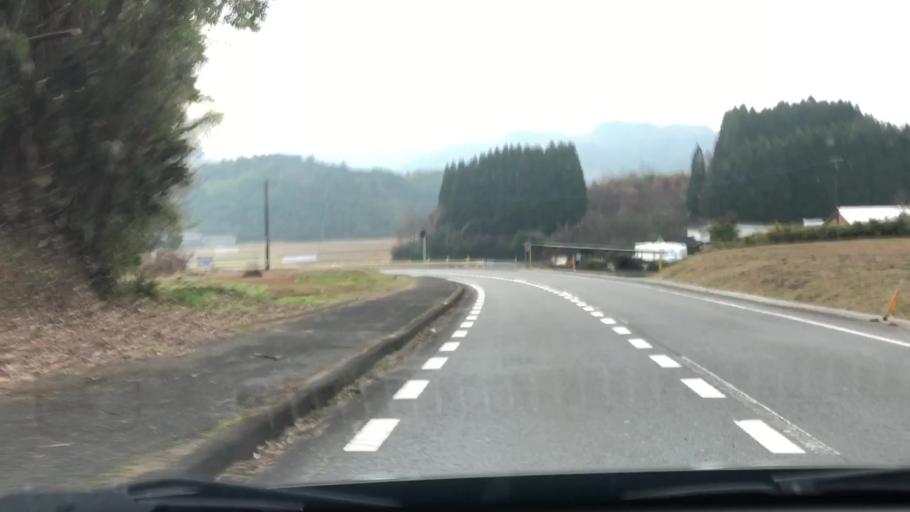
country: JP
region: Oita
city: Takedamachi
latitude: 32.9759
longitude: 131.5595
